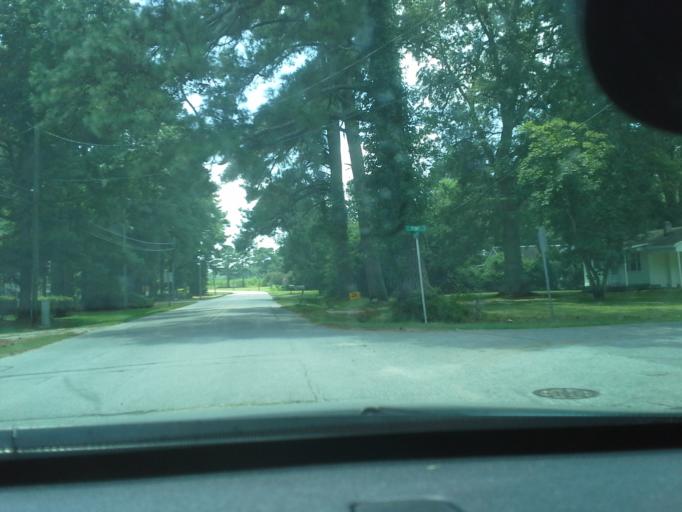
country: US
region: North Carolina
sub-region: Washington County
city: Plymouth
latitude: 35.8473
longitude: -76.7604
